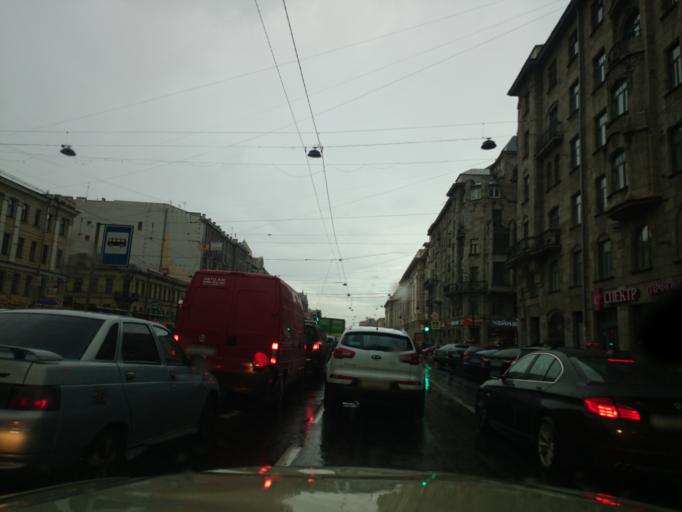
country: RU
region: St.-Petersburg
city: Centralniy
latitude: 59.9259
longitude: 30.3580
